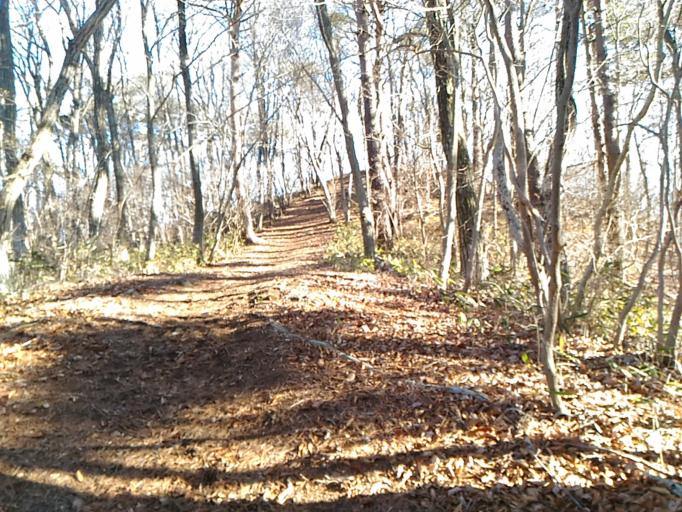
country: JP
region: Fukushima
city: Ishikawa
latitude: 36.9567
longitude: 140.5834
